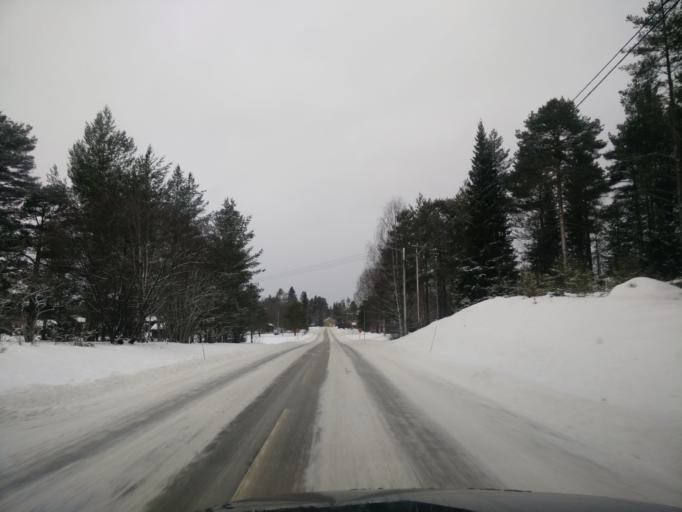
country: SE
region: Jaemtland
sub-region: Braecke Kommun
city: Braecke
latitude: 62.3966
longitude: 15.2155
